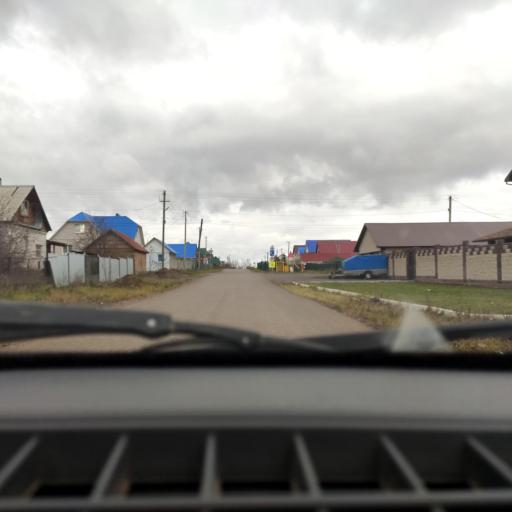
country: RU
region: Bashkortostan
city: Mikhaylovka
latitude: 54.8177
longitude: 55.8901
